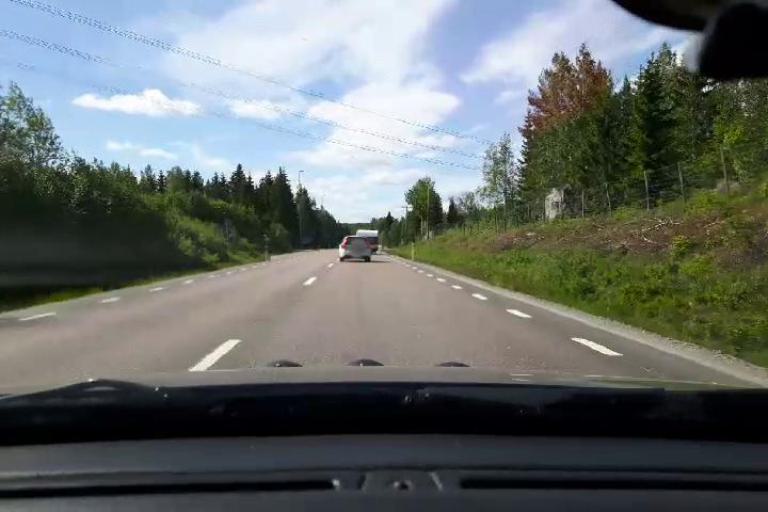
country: SE
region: Gaevleborg
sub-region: Bollnas Kommun
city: Kilafors
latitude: 61.2898
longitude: 16.5059
